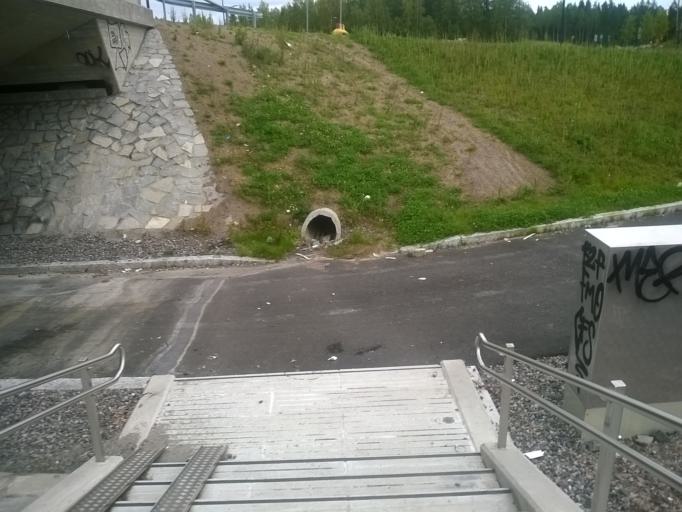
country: FI
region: Uusimaa
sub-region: Helsinki
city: Teekkarikylae
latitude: 60.2594
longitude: 24.8945
